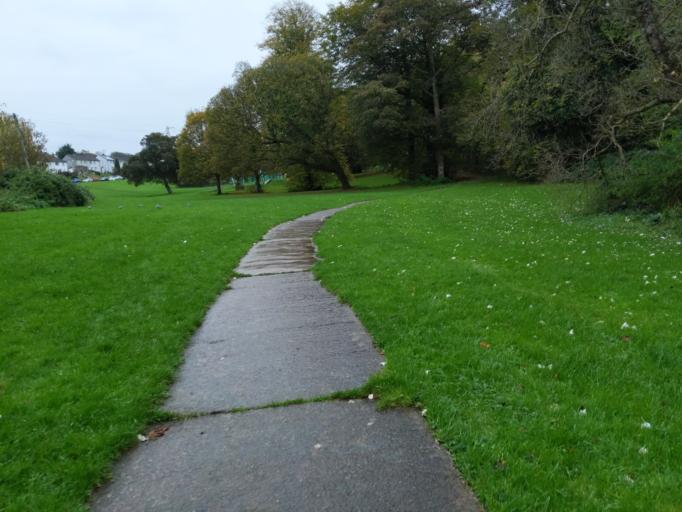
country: GB
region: England
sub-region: Plymouth
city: Plymouth
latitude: 50.4143
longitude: -4.1464
